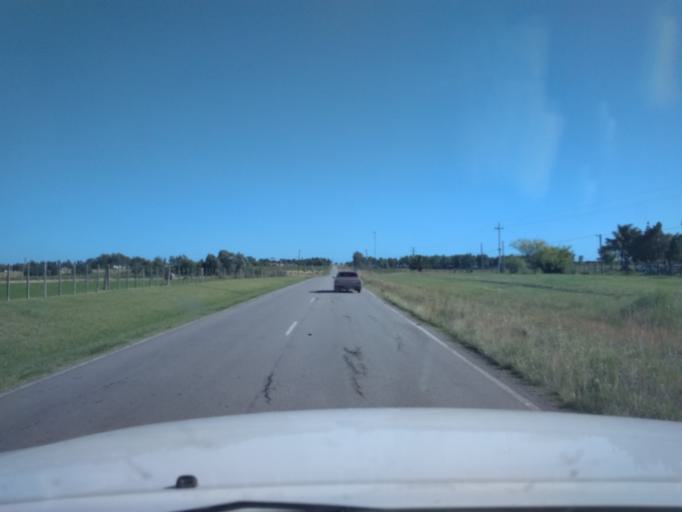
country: UY
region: Canelones
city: San Ramon
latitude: -34.3162
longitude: -55.9593
